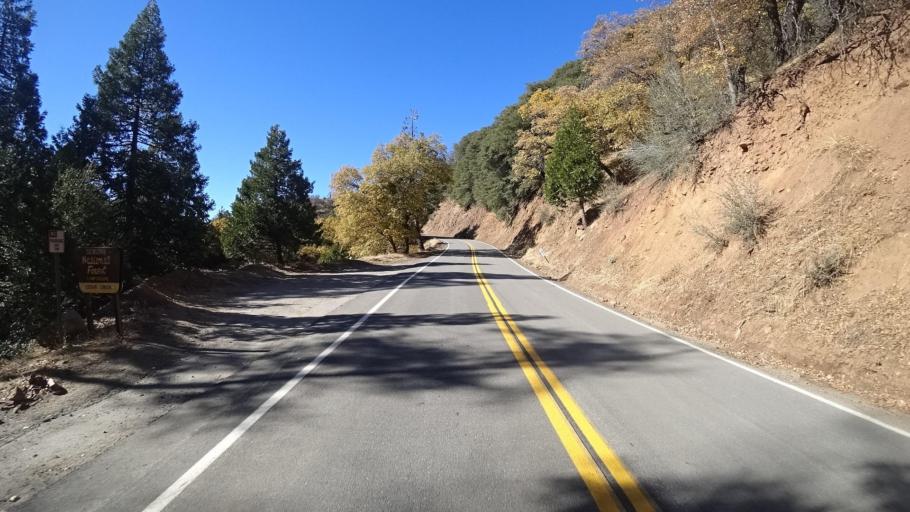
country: US
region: California
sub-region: Kern County
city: Alta Sierra
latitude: 35.7490
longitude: -118.5837
